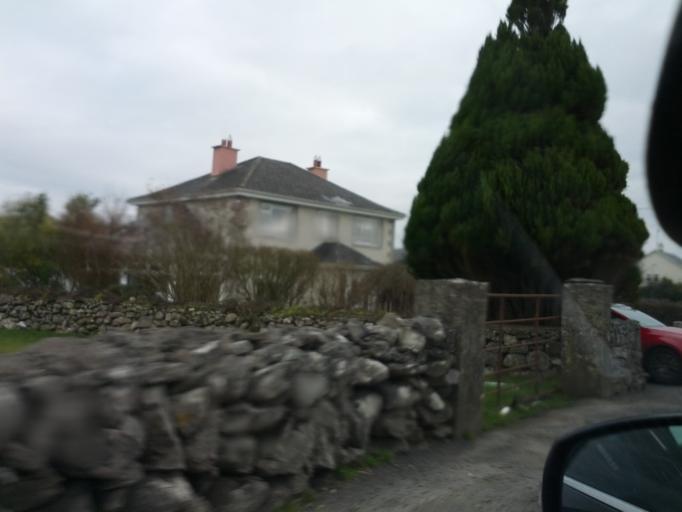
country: IE
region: Connaught
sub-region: County Galway
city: Athenry
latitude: 53.2586
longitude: -8.7391
